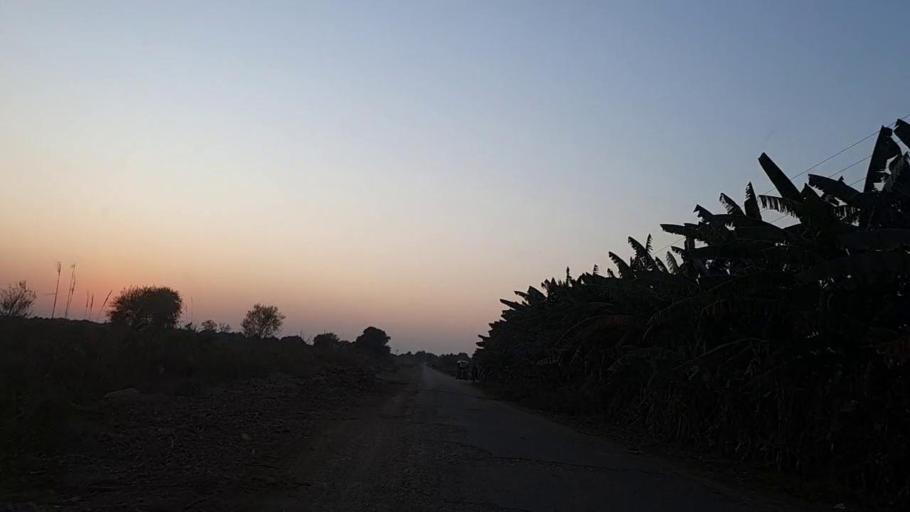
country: PK
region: Sindh
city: Hala
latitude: 25.9592
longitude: 68.4109
